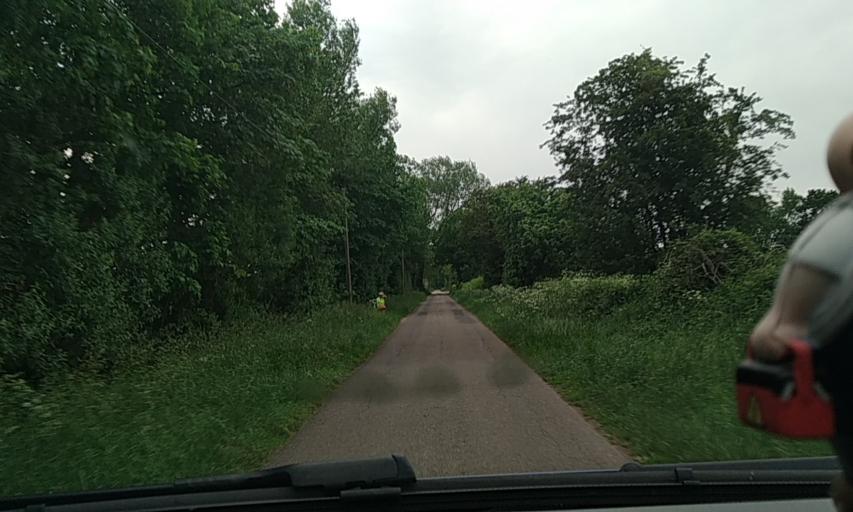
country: DE
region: Schleswig-Holstein
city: Borm
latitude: 54.3899
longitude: 9.3862
